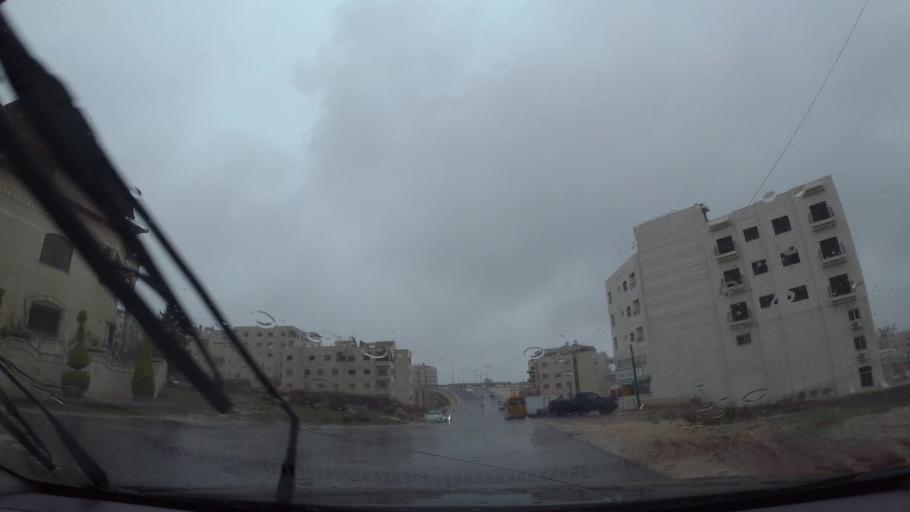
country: JO
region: Amman
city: Al Jubayhah
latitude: 32.0137
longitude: 35.8895
